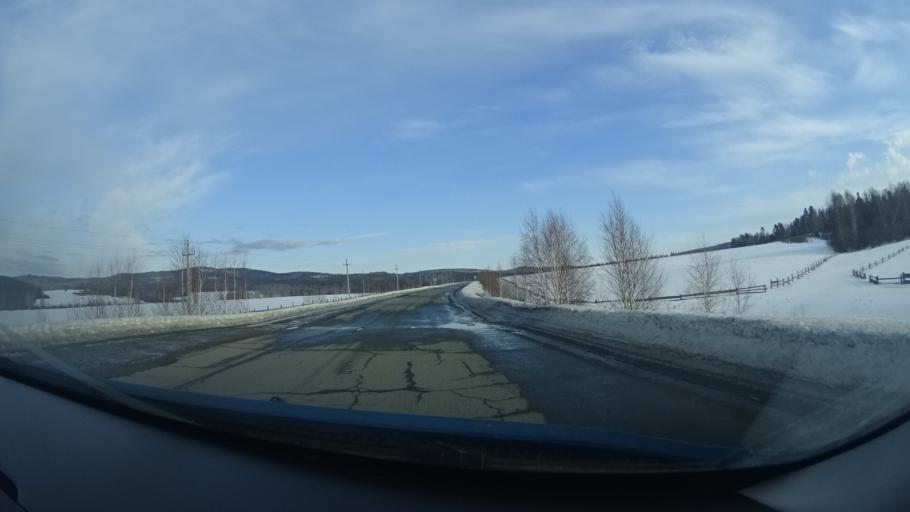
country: RU
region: Bashkortostan
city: Lomovka
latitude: 53.7214
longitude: 58.2518
